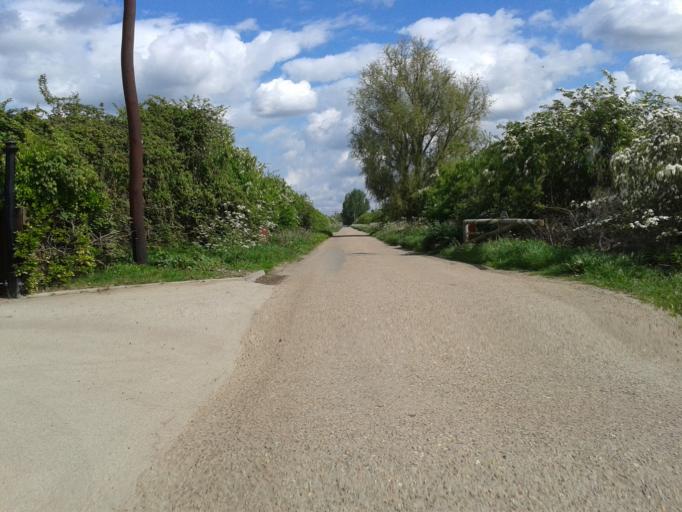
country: GB
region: England
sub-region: Cambridgeshire
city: Waterbeach
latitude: 52.2276
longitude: 0.1650
